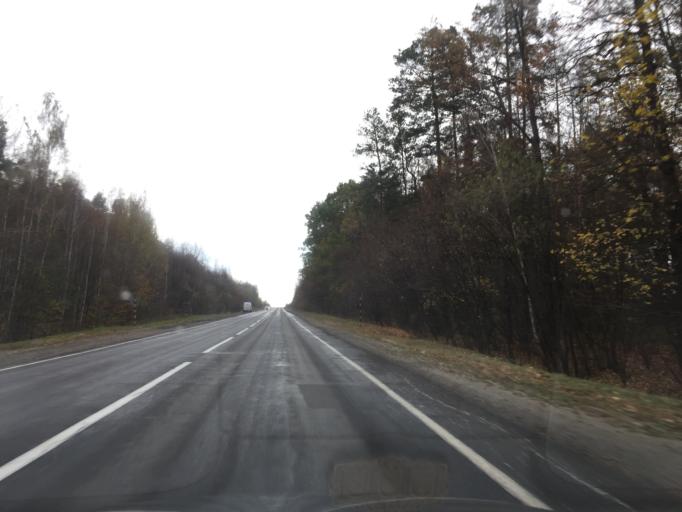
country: BY
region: Gomel
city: Gomel
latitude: 52.4097
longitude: 30.8289
